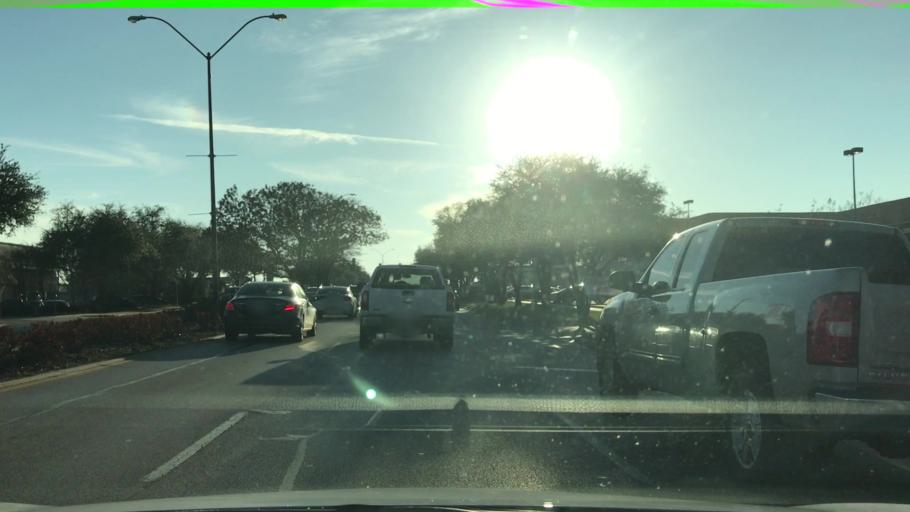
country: US
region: Texas
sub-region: Tarrant County
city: Westworth
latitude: 32.7276
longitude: -97.4183
